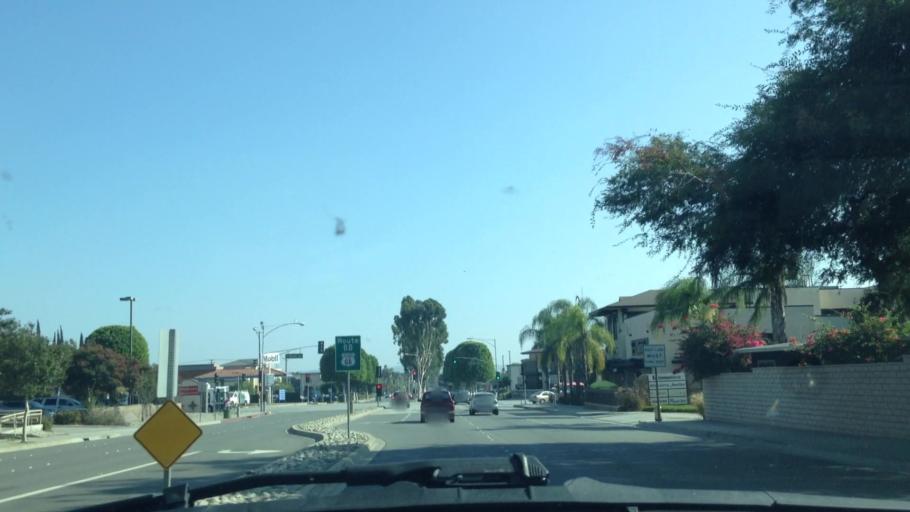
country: US
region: California
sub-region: Los Angeles County
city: Glendora
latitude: 34.1299
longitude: -117.8727
